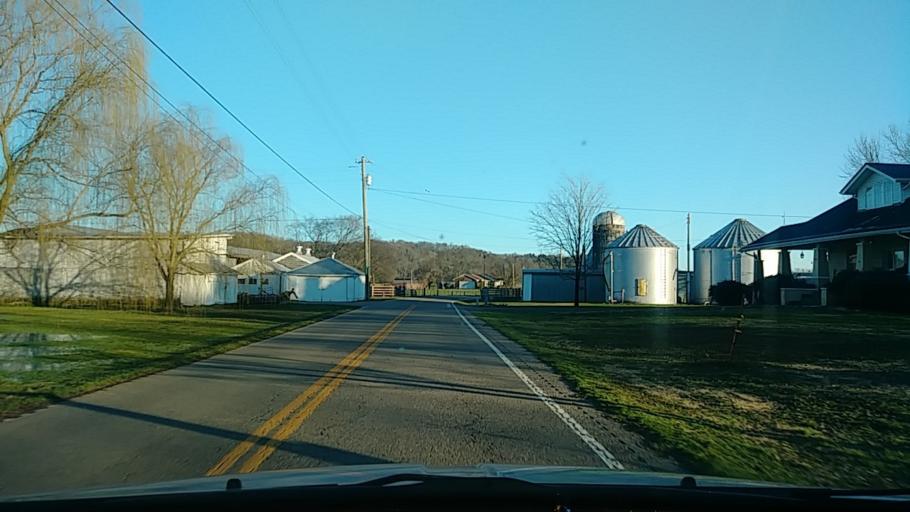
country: US
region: Tennessee
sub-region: Jefferson County
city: White Pine
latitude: 36.1369
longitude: -83.1365
